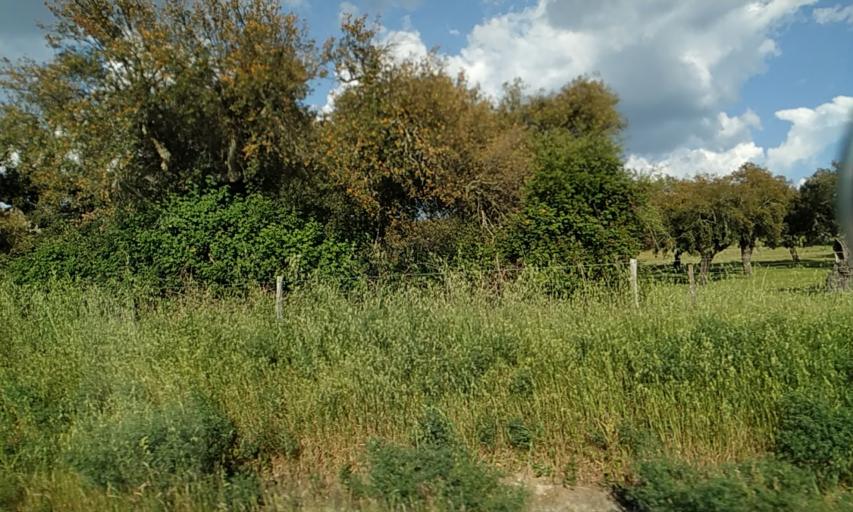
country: PT
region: Portalegre
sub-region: Portalegre
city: Urra
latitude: 39.2242
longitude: -7.4563
